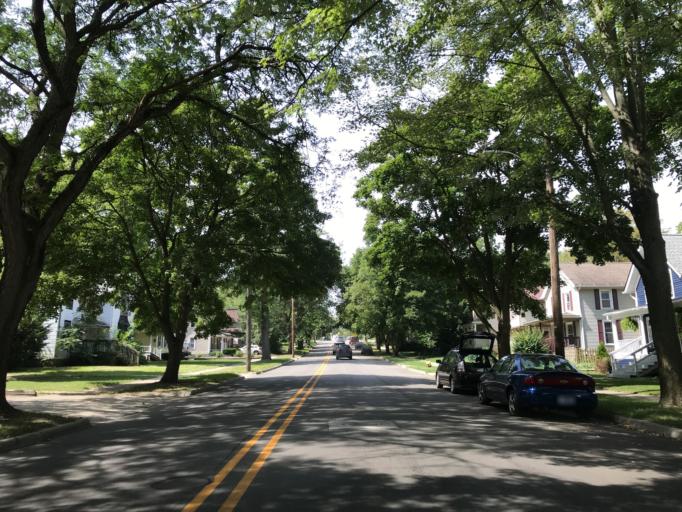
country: US
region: Michigan
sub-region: Washtenaw County
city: Ypsilanti
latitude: 42.2410
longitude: -83.6211
